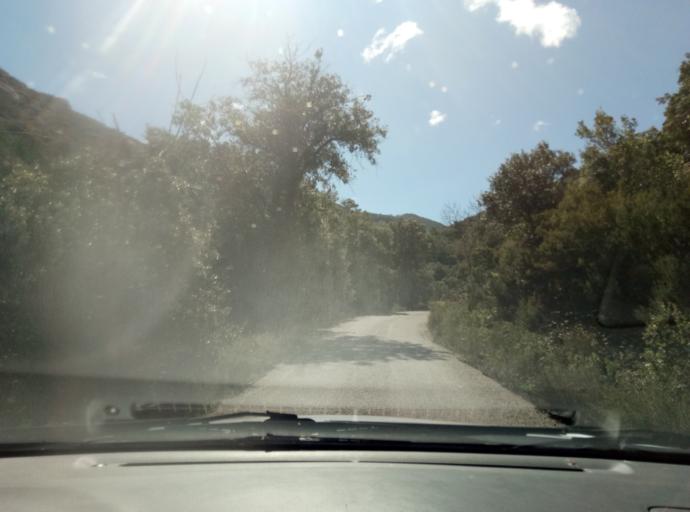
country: ES
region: Catalonia
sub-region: Provincia de Tarragona
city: Vimbodi
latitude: 41.3567
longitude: 1.0613
